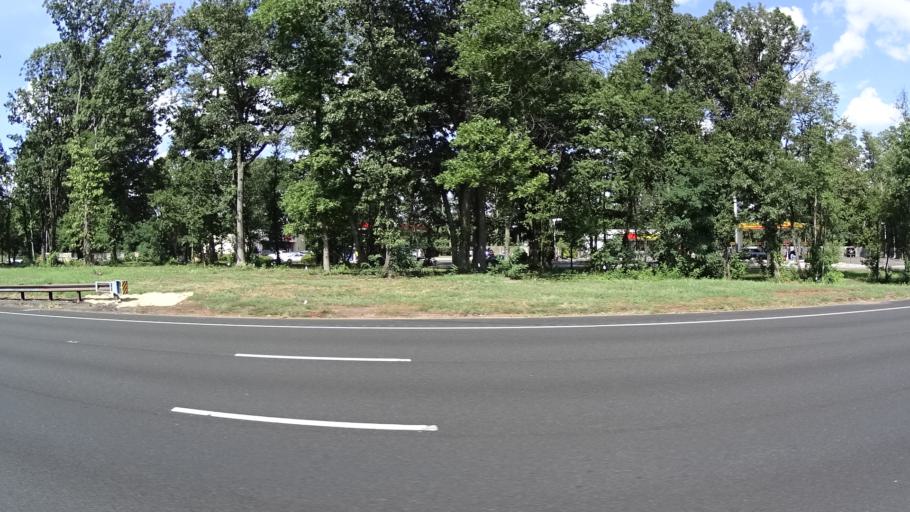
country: US
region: New Jersey
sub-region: Middlesex County
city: Iselin
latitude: 40.5820
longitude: -74.3307
